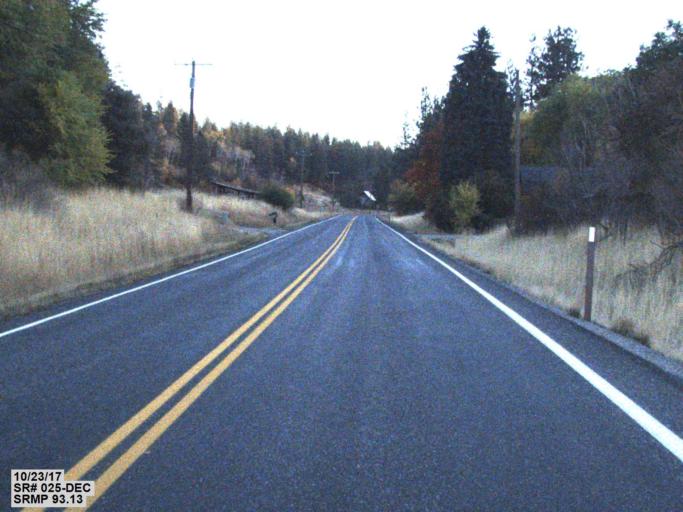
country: US
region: Washington
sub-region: Stevens County
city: Kettle Falls
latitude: 48.7351
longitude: -118.0485
